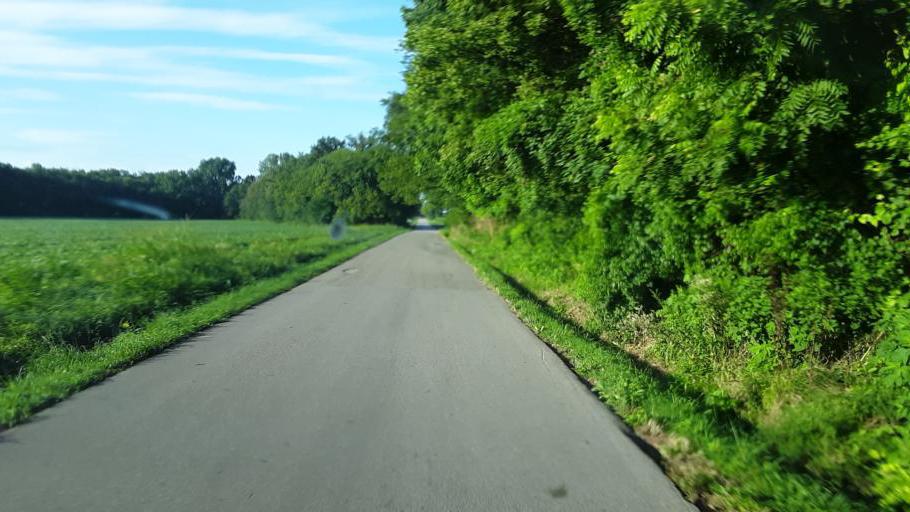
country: US
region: Kentucky
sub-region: Todd County
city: Elkton
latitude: 36.7315
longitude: -87.1676
